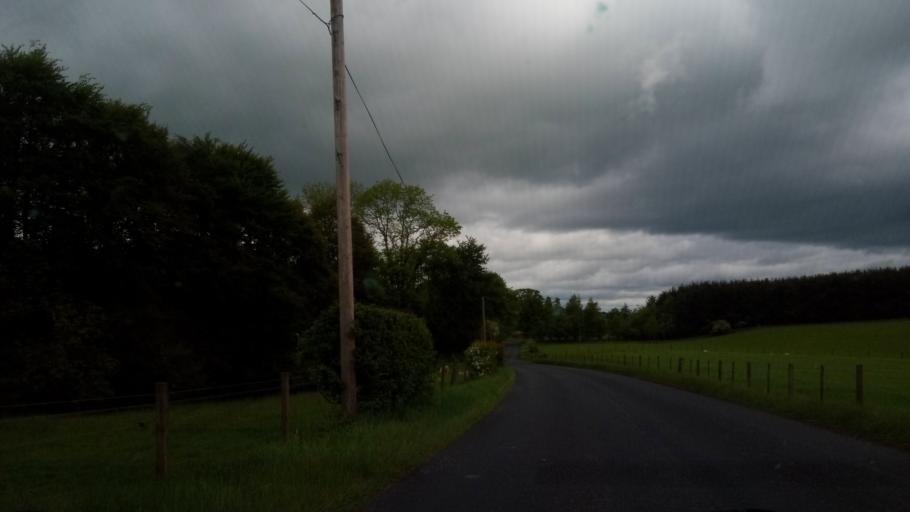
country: GB
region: Scotland
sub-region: The Scottish Borders
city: Hawick
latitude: 55.4671
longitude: -2.7397
